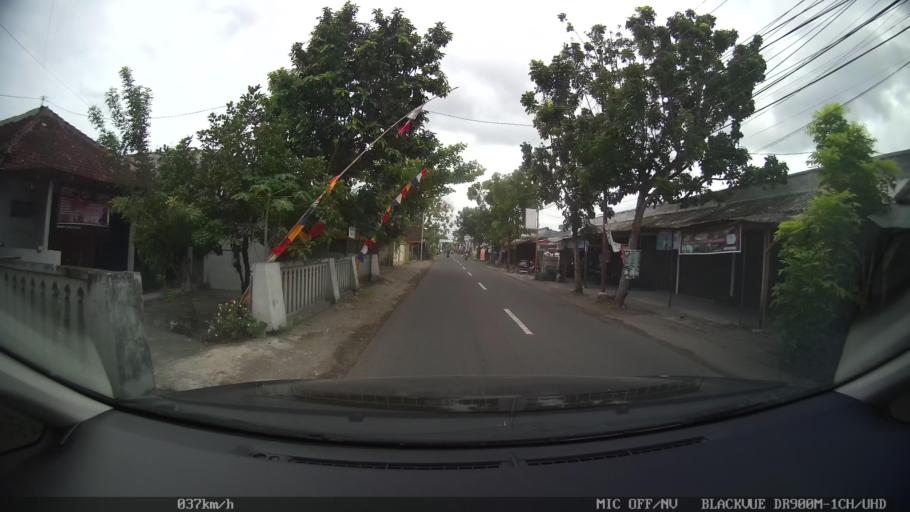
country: ID
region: Daerah Istimewa Yogyakarta
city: Depok
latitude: -7.8237
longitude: 110.4145
